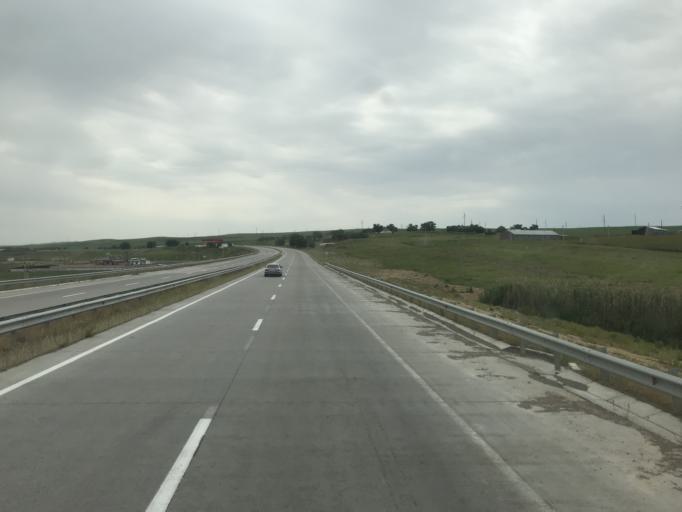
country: KZ
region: Ongtustik Qazaqstan
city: Qazyqurt
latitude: 41.8689
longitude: 69.4189
